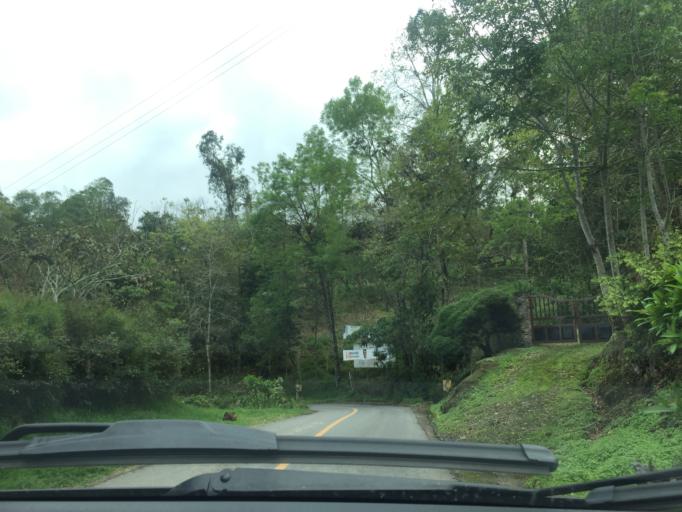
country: CO
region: Cundinamarca
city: Supata
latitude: 5.0578
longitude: -74.2351
